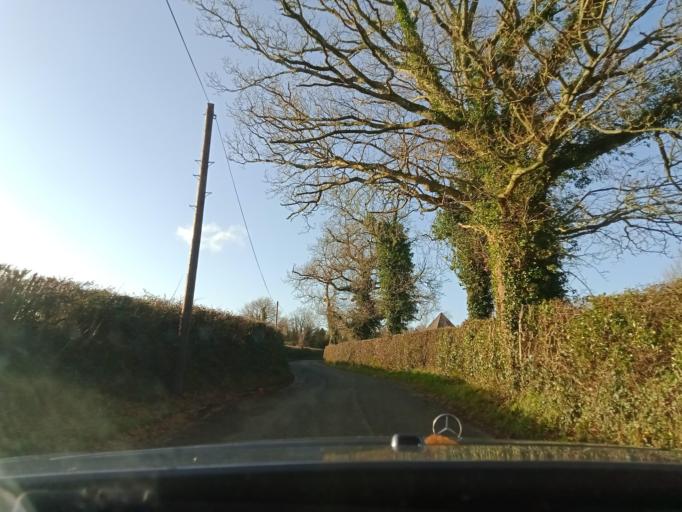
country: IE
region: Leinster
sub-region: Kilkenny
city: Callan
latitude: 52.5001
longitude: -7.3779
